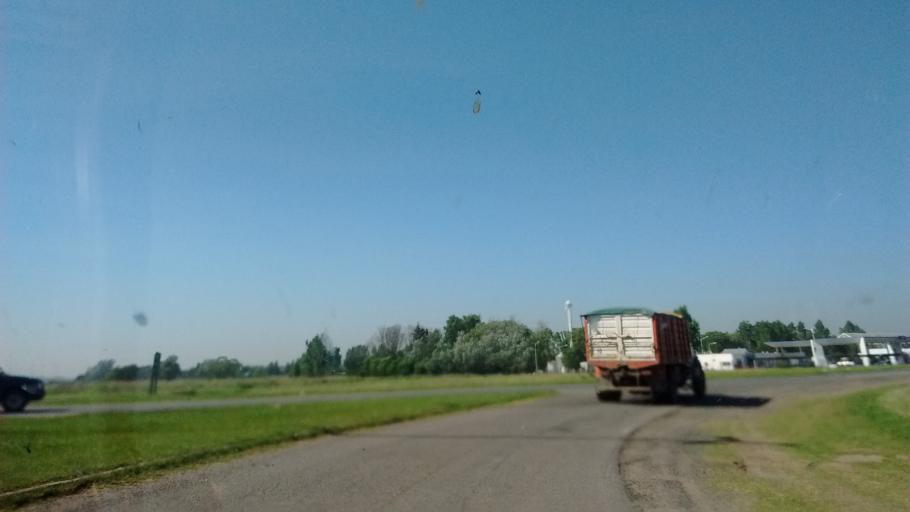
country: AR
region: Buenos Aires
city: General Villegas
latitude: -35.0355
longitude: -62.9879
